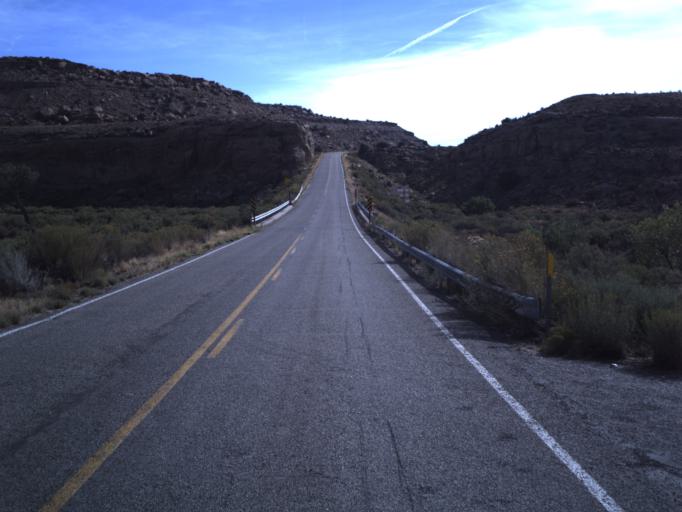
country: US
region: Utah
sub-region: San Juan County
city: Blanding
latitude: 37.4191
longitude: -109.4440
